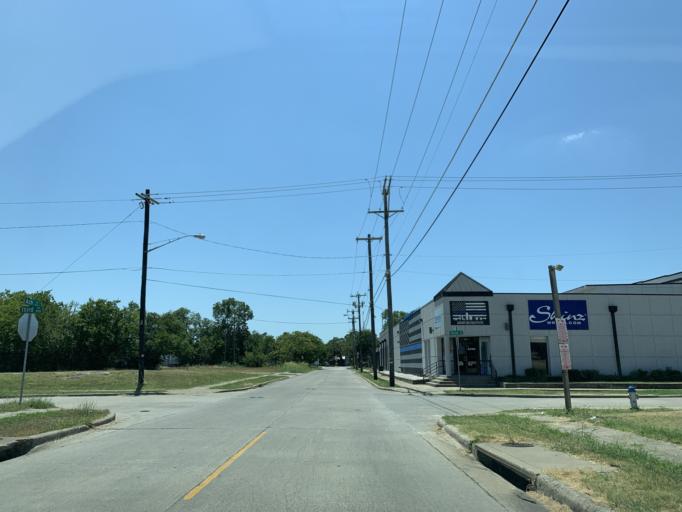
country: US
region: Texas
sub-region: Dallas County
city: Dallas
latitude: 32.7803
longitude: -96.7690
